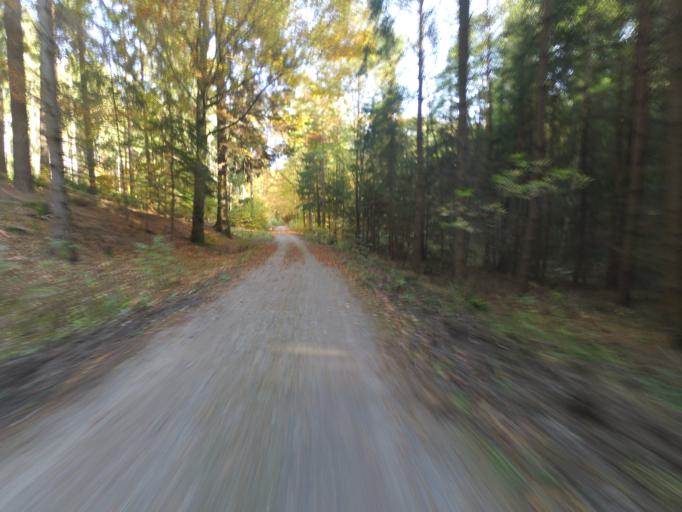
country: DE
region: Saxony
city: Radeberg
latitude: 51.0935
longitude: 13.8521
